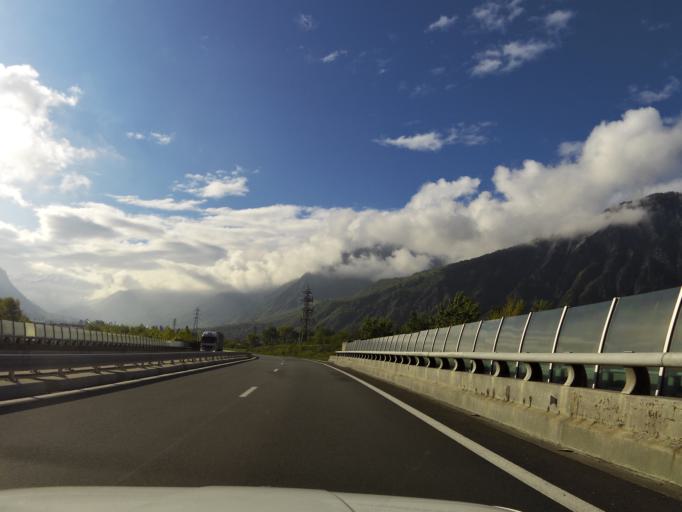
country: FR
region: Rhone-Alpes
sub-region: Departement de la Savoie
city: Saint-Jean-de-Maurienne
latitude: 45.2799
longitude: 6.3576
